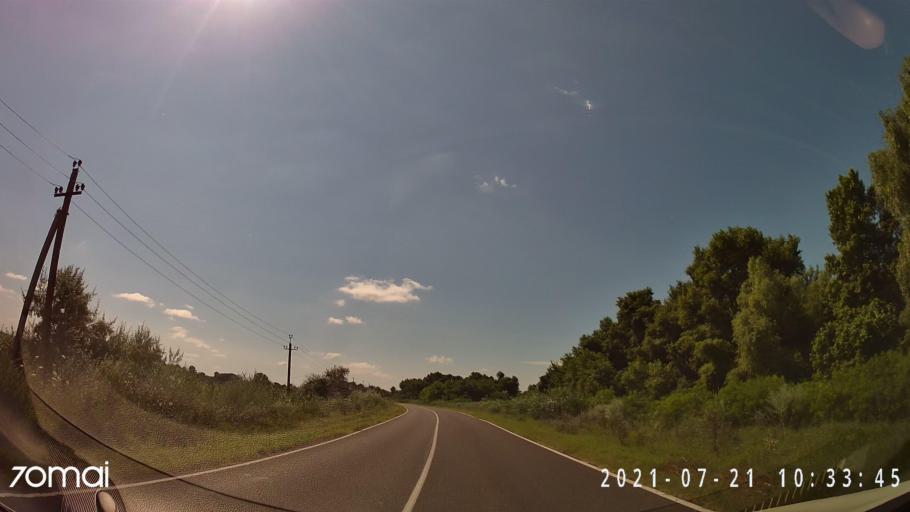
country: RO
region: Tulcea
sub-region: Oras Isaccea
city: Isaccea
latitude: 45.2997
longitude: 28.4372
